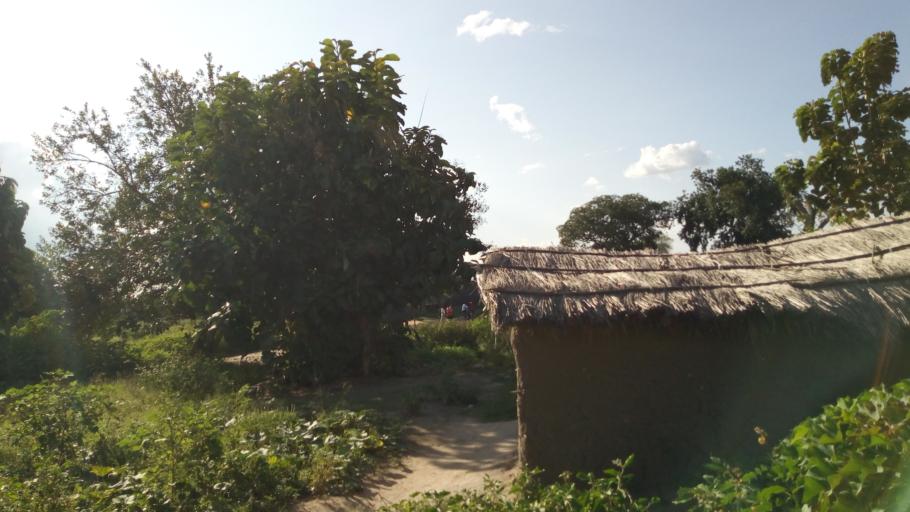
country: UG
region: Northern Region
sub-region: Arua District
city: Arua
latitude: 3.0756
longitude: 31.2836
